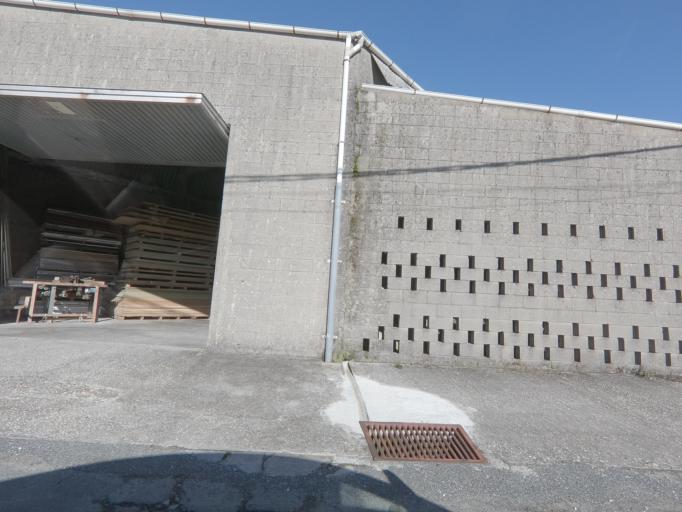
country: ES
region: Galicia
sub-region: Provincia da Coruna
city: Ribeira
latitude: 42.7140
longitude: -8.4462
